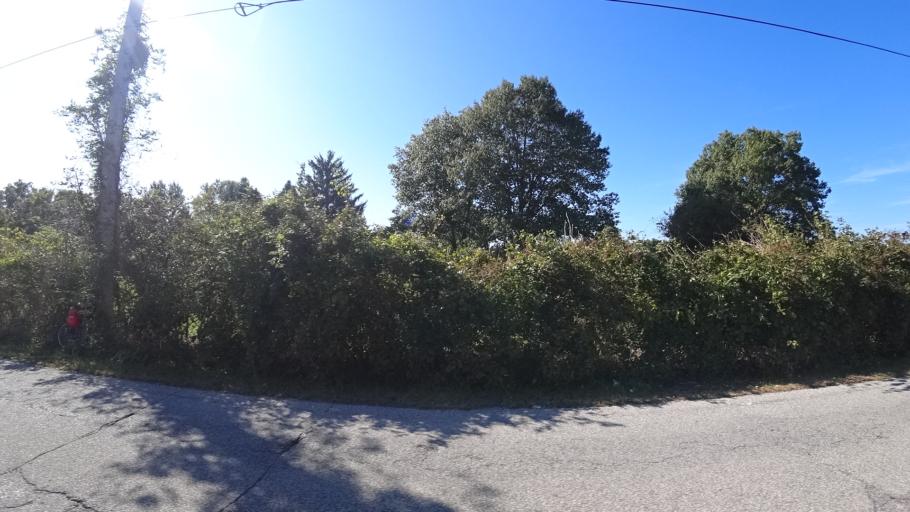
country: US
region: Indiana
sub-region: LaPorte County
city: Trail Creek
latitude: 41.7099
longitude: -86.8404
